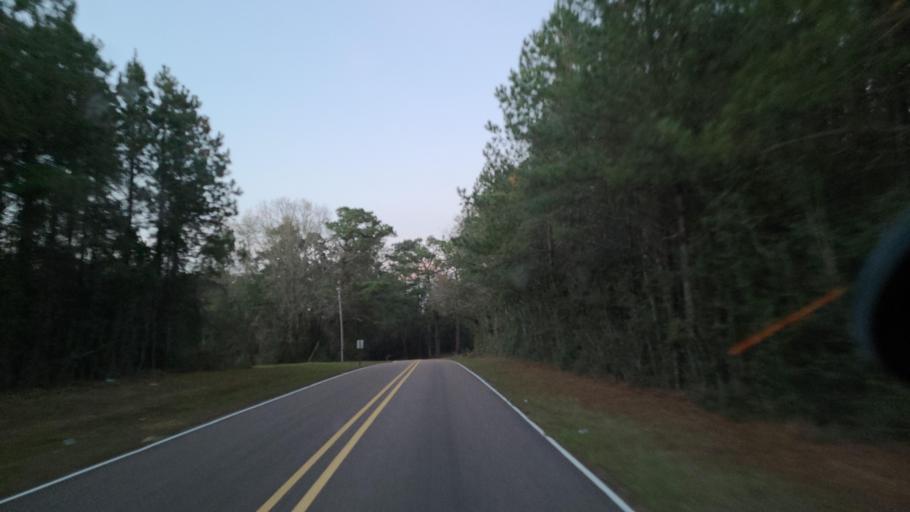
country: US
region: Mississippi
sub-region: Forrest County
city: Hattiesburg
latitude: 31.2255
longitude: -89.2356
